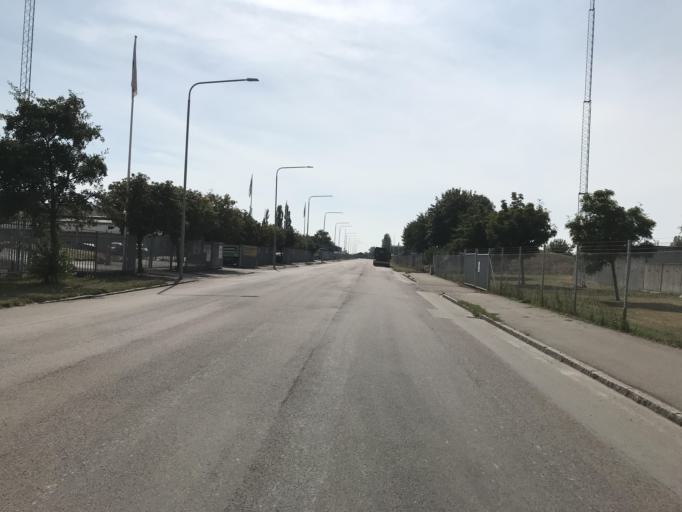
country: SE
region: Skane
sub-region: Landskrona
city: Landskrona
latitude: 55.8650
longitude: 12.8513
